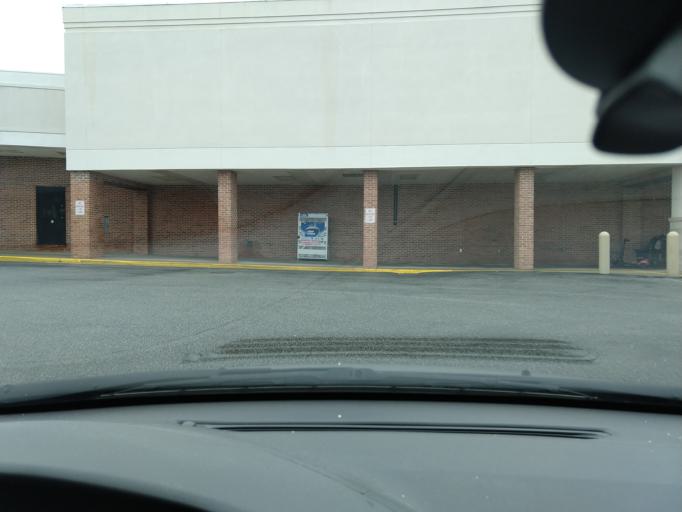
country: US
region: Alabama
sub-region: Houston County
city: Dothan
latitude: 31.2589
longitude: -85.4323
